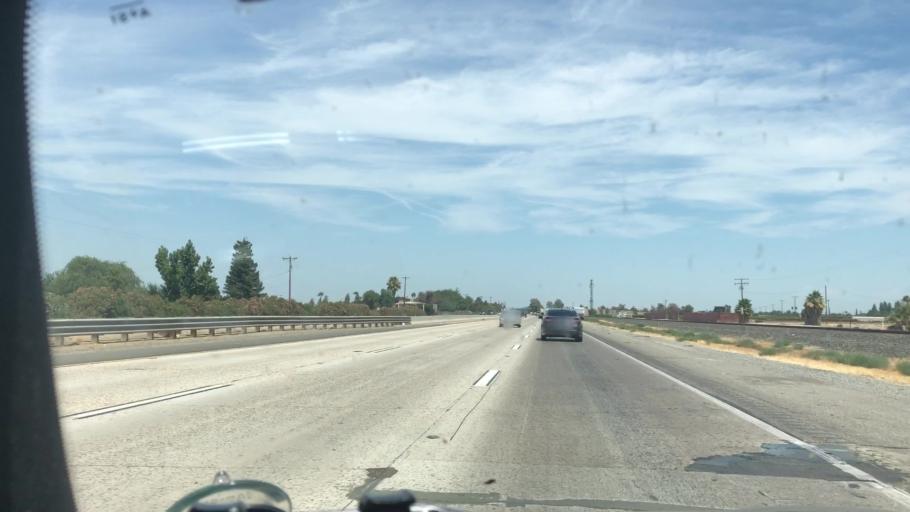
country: US
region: California
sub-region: Kern County
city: McFarland
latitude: 35.6632
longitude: -119.2235
